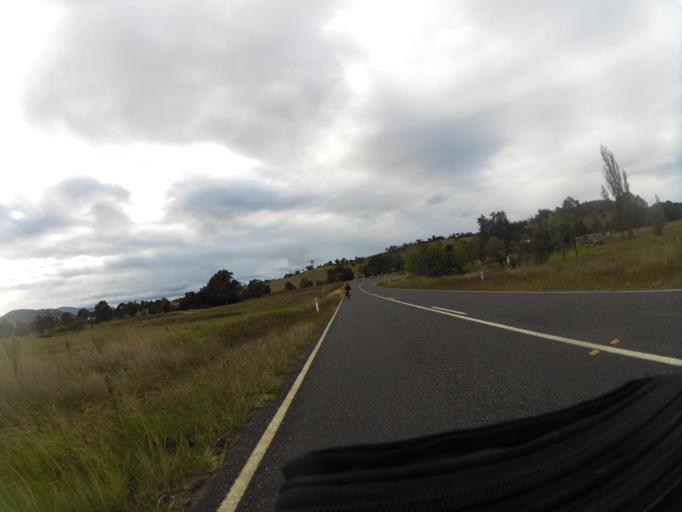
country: AU
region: New South Wales
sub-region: Snowy River
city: Jindabyne
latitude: -36.1249
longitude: 147.9863
